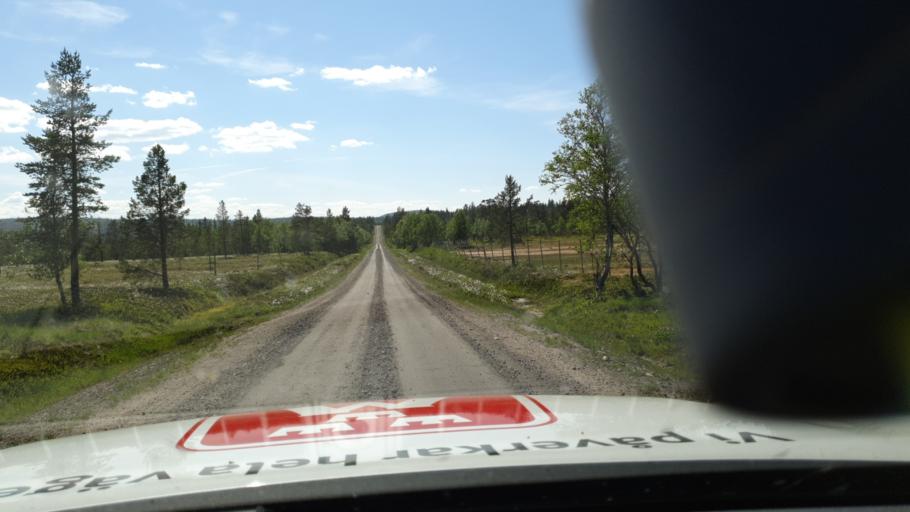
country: NO
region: Hedmark
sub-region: Engerdal
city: Engerdal
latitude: 62.1369
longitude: 12.9315
